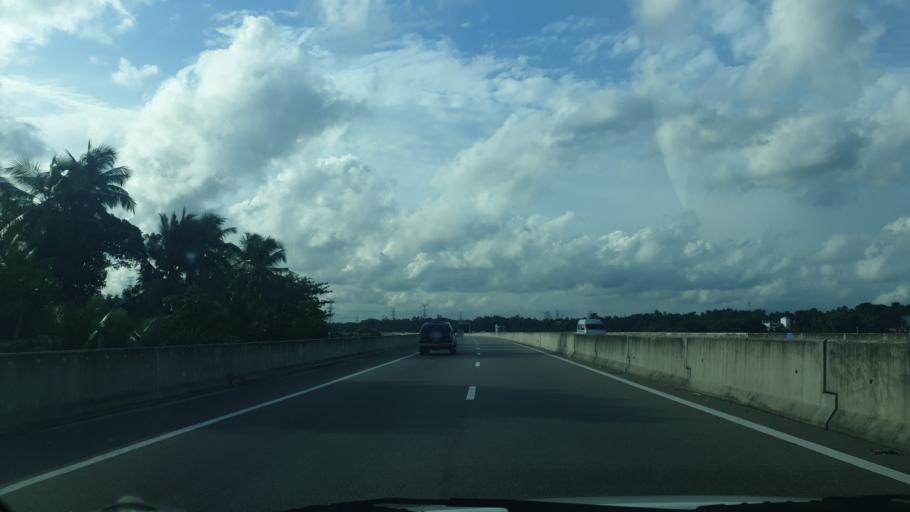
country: LK
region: Western
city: Mulleriyawa
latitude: 6.9559
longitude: 79.9764
